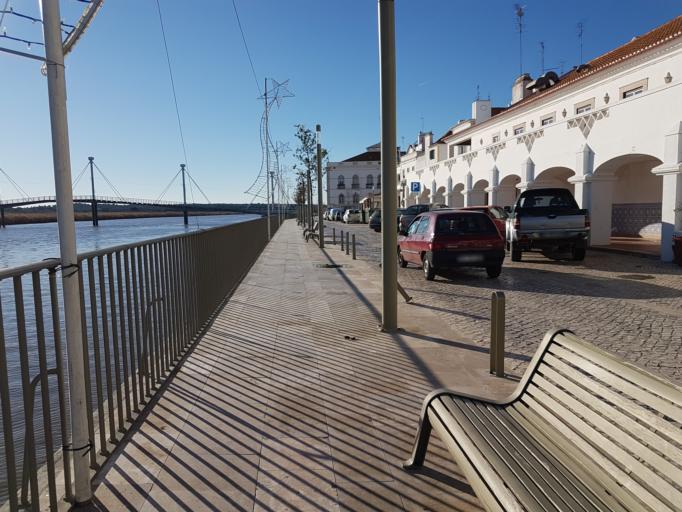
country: PT
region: Setubal
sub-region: Alcacer do Sal
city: Alcacer do Sal
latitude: 38.3709
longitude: -8.5111
